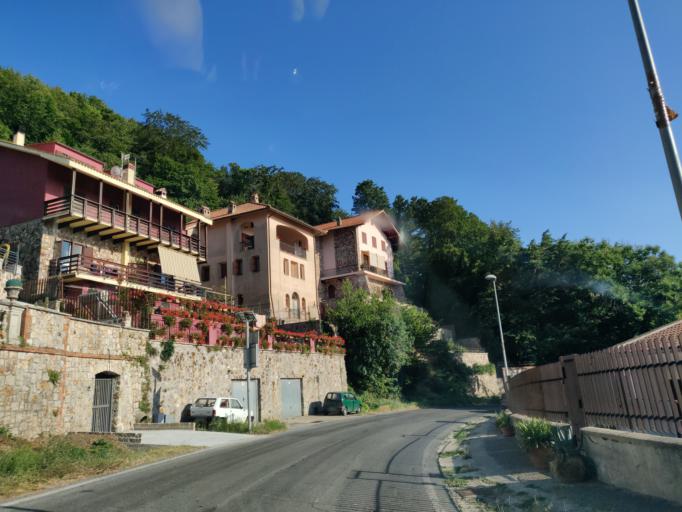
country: IT
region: Latium
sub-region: Citta metropolitana di Roma Capitale
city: Allumiere
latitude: 42.1565
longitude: 11.9073
